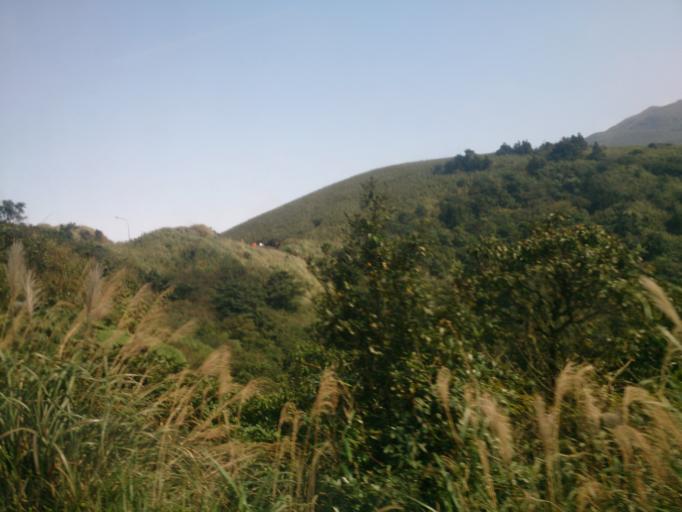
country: TW
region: Taipei
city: Taipei
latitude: 25.1798
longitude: 121.5447
